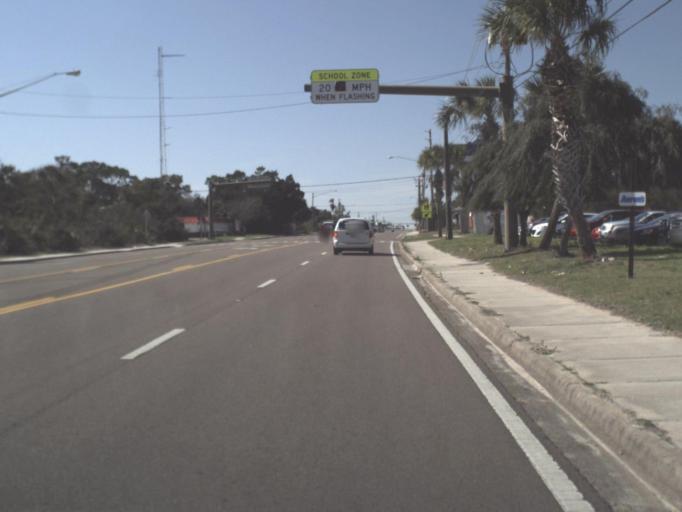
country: US
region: Florida
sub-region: Bay County
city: Panama City Beach
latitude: 30.1987
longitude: -85.8369
